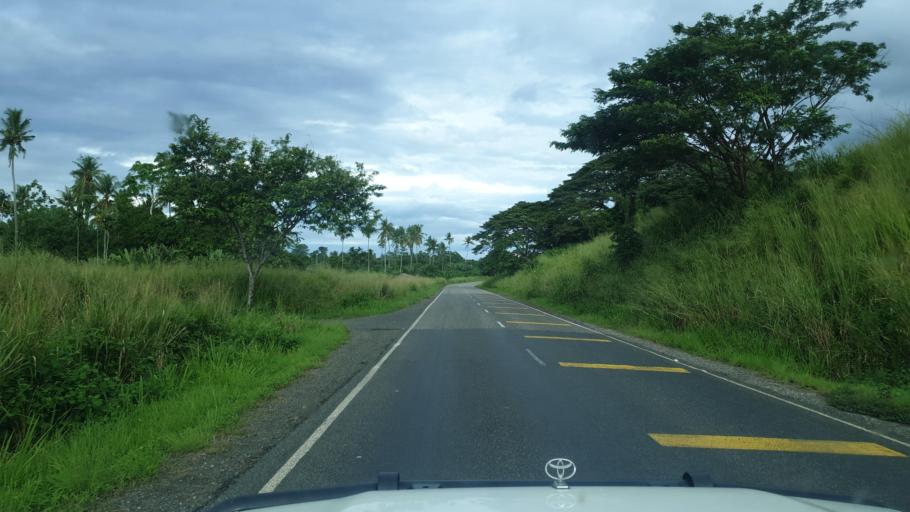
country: PG
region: National Capital
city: Port Moresby
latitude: -9.1026
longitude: 147.1389
